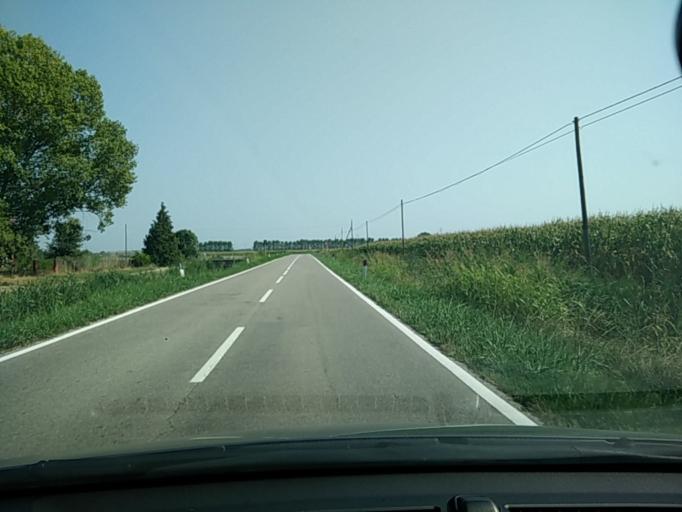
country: IT
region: Veneto
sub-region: Provincia di Venezia
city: La Salute di Livenza
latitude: 45.6277
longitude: 12.8380
